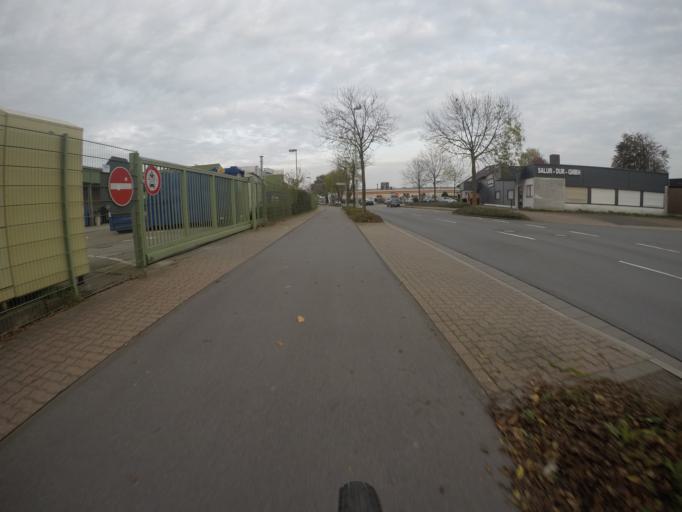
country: DE
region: North Rhine-Westphalia
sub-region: Regierungsbezirk Dusseldorf
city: Bocholt
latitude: 51.8205
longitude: 6.6039
